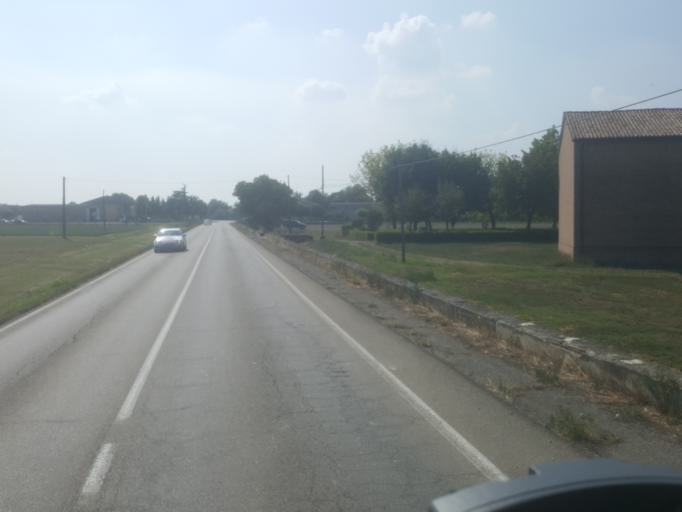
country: IT
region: Emilia-Romagna
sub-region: Provincia di Parma
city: Colorno
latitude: 44.9610
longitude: 10.3878
